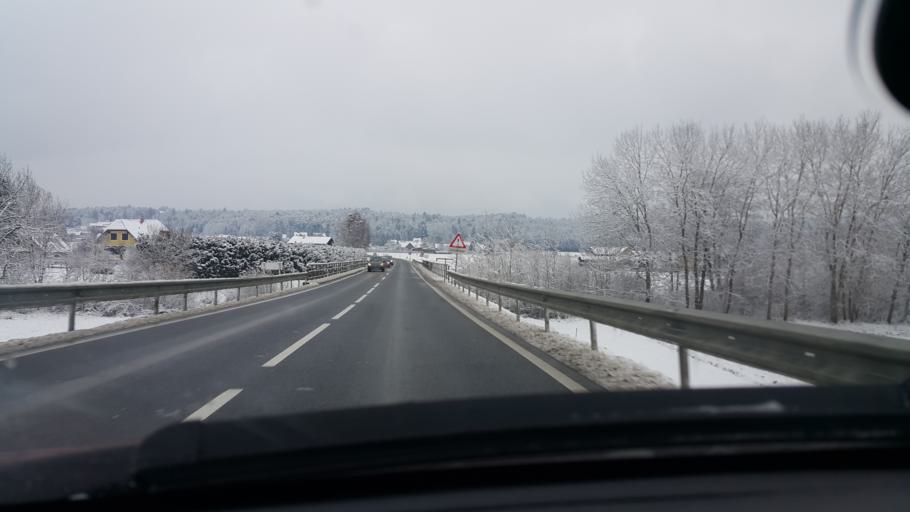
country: AT
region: Styria
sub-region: Politischer Bezirk Voitsberg
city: Mooskirchen
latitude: 47.0105
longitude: 15.2730
